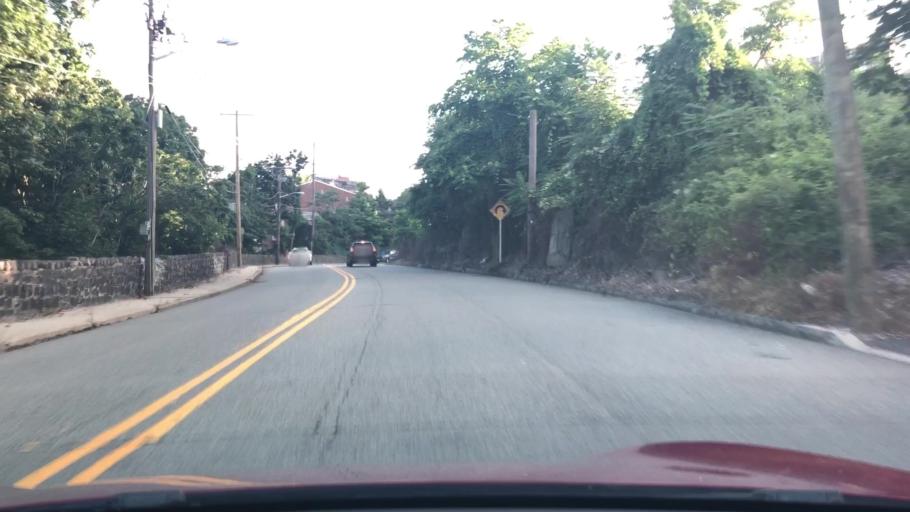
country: US
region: New Jersey
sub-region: Bergen County
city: Edgewater
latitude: 40.8304
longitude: -73.9753
